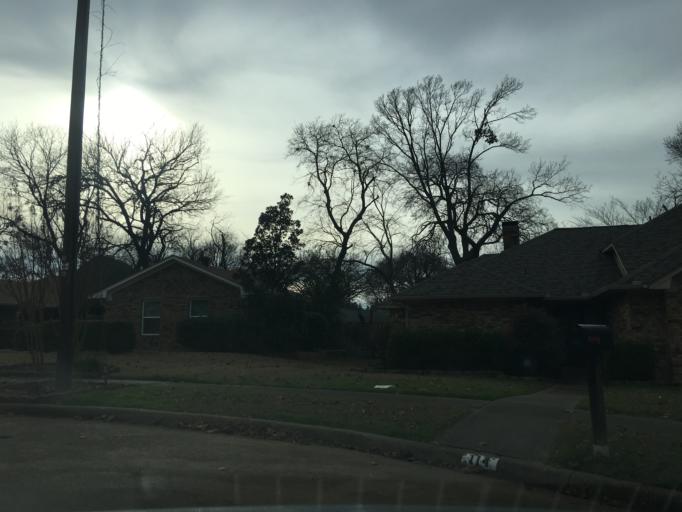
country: US
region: Texas
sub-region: Collin County
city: McKinney
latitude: 33.1956
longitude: -96.6430
